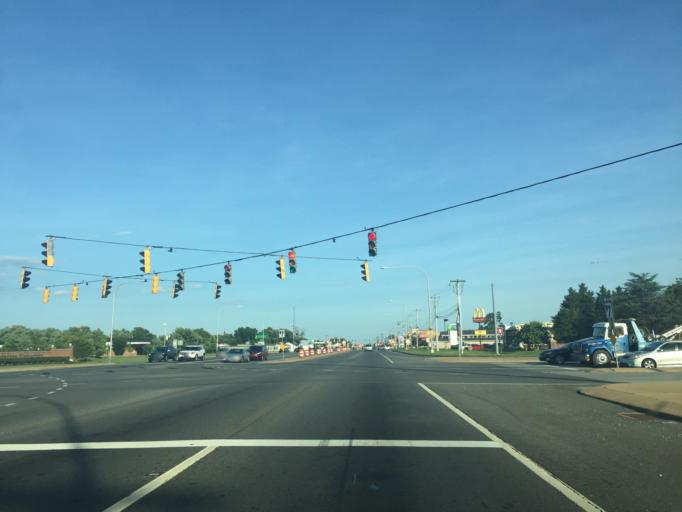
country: US
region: Delaware
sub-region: Kent County
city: Cheswold
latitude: 39.2002
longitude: -75.5562
